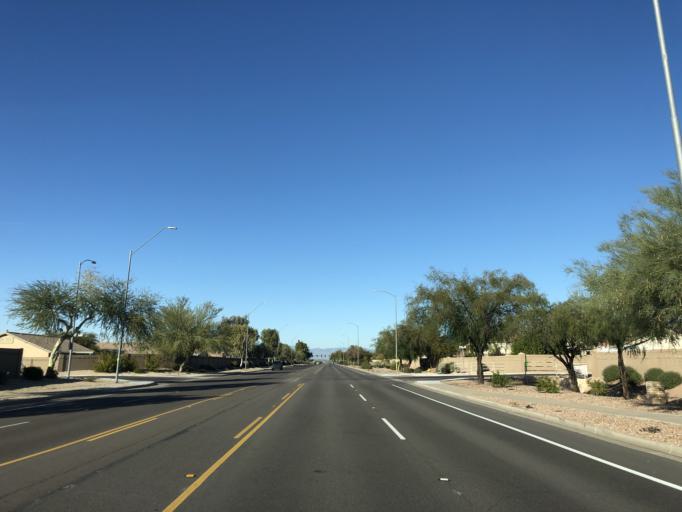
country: US
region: Arizona
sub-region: Maricopa County
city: Sun City West
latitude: 33.6847
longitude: -112.2898
